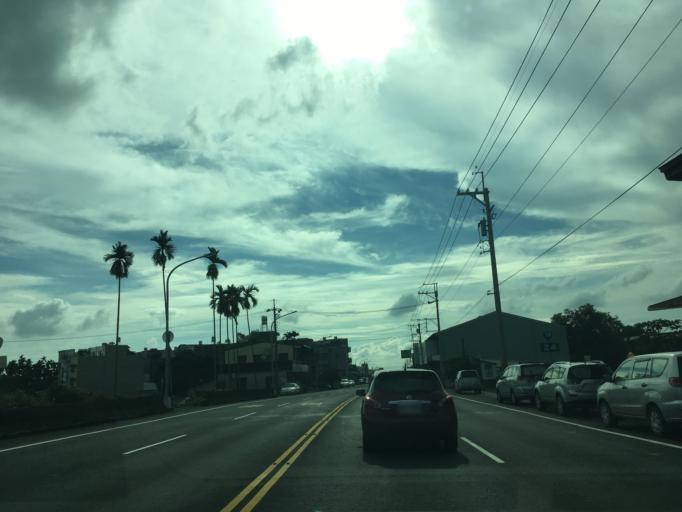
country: TW
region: Taiwan
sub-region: Chiayi
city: Jiayi Shi
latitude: 23.4424
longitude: 120.5148
